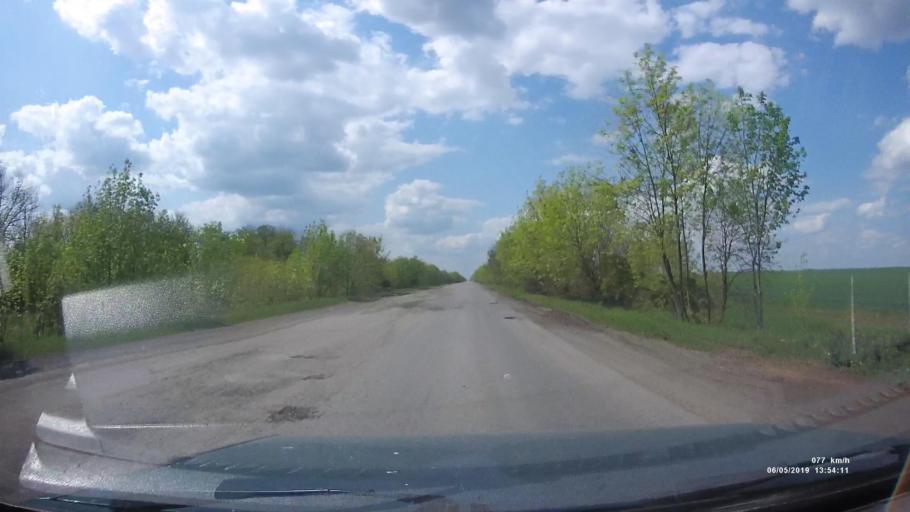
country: RU
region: Rostov
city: Melikhovskaya
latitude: 47.6730
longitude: 40.4508
